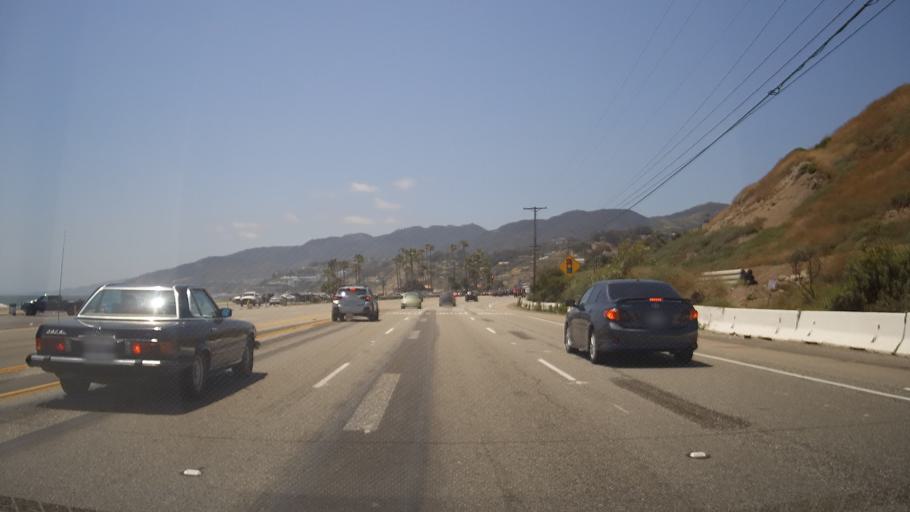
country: US
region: California
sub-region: Los Angeles County
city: Santa Monica
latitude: 34.0333
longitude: -118.5326
